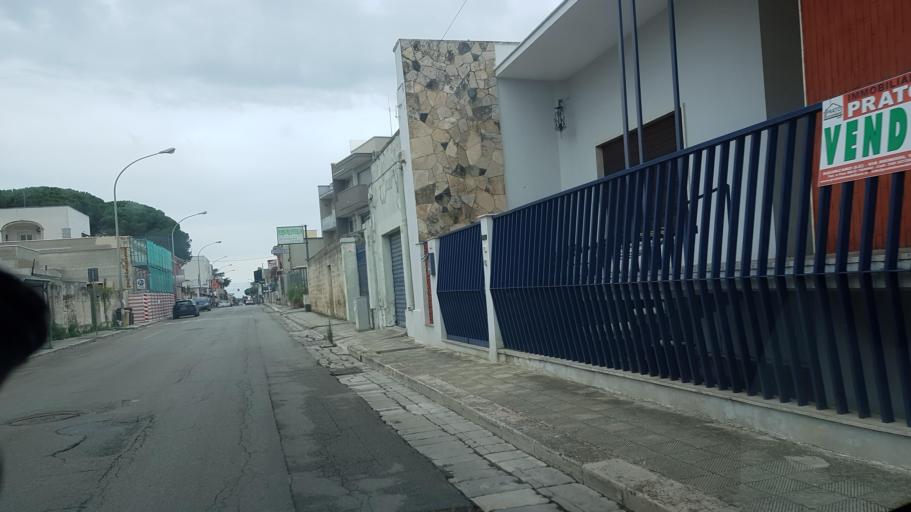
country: IT
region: Apulia
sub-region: Provincia di Lecce
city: Squinzano
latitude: 40.4378
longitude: 18.0386
